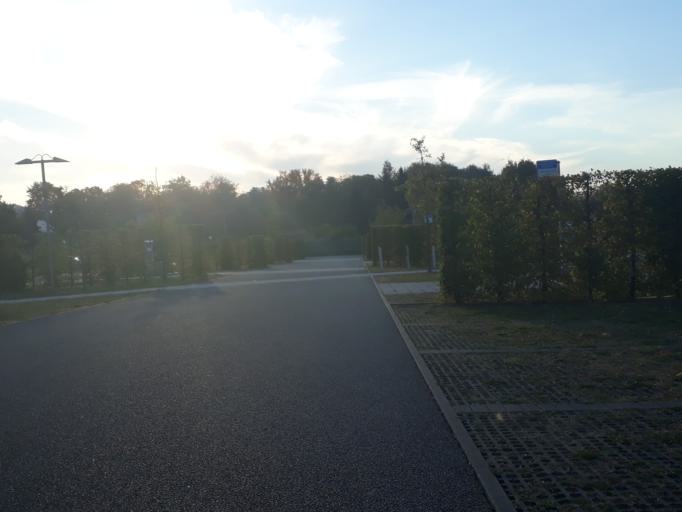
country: DE
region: Saxony
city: Heidenau
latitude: 51.0137
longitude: 13.8644
